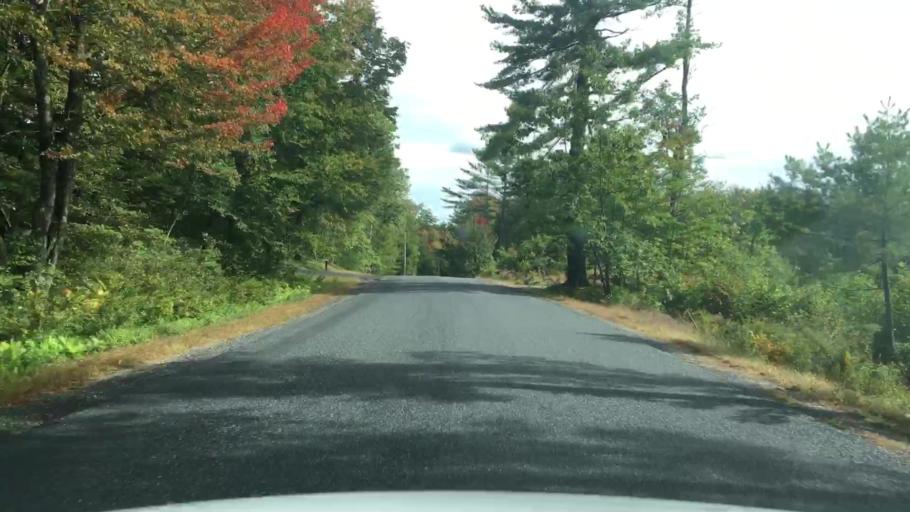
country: US
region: Maine
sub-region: Androscoggin County
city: Lisbon Falls
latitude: 43.9739
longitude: -70.0875
